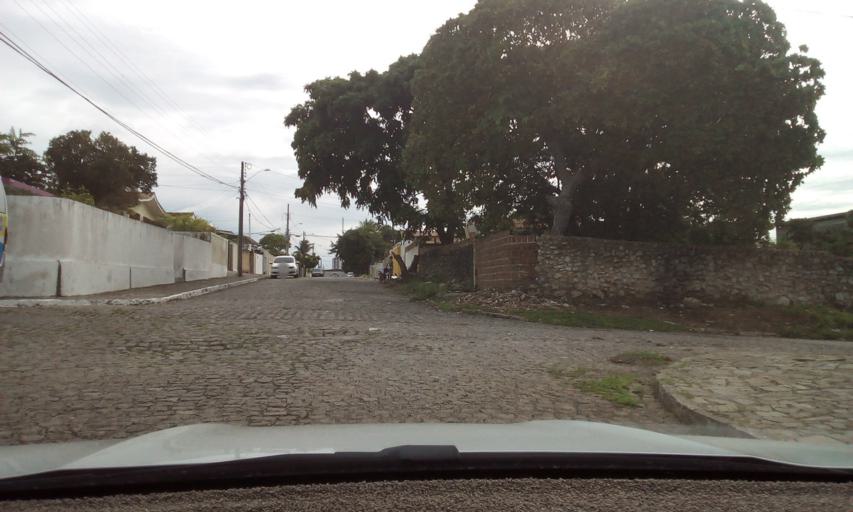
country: BR
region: Paraiba
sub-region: Joao Pessoa
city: Joao Pessoa
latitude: -7.1066
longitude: -34.8537
